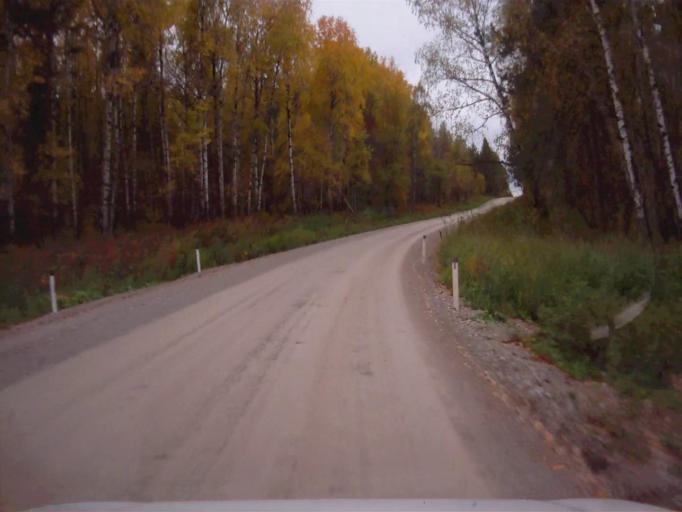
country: RU
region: Chelyabinsk
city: Nyazepetrovsk
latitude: 56.0689
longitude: 59.4327
